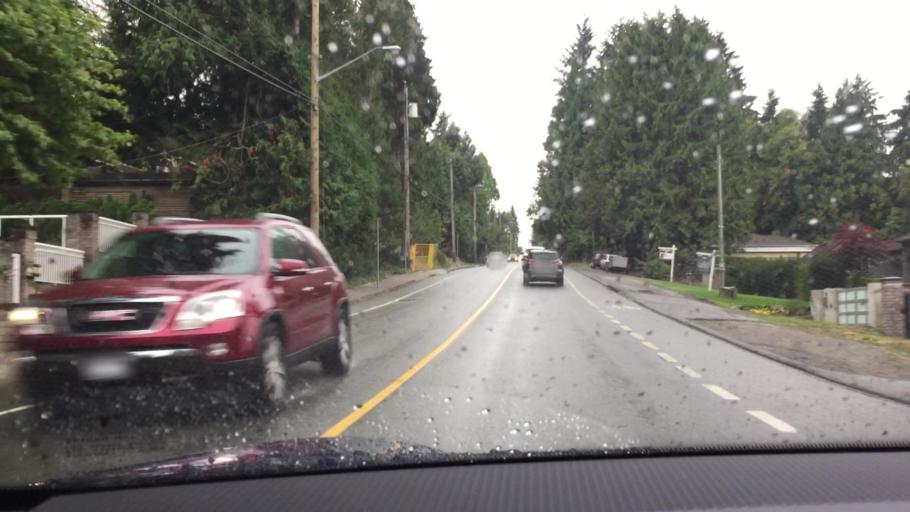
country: CA
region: British Columbia
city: Burnaby
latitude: 49.2336
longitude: -122.9579
